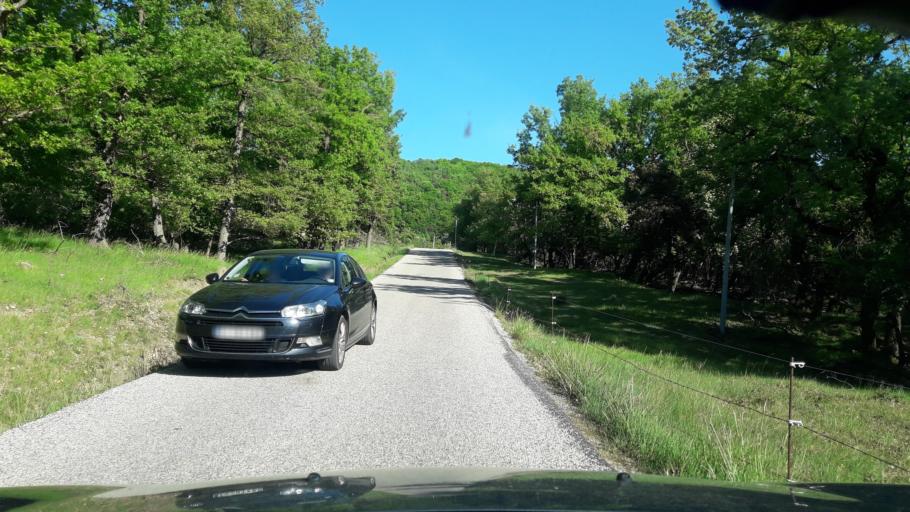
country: FR
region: Rhone-Alpes
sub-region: Departement de la Drome
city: Grane
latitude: 44.7061
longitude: 4.8835
